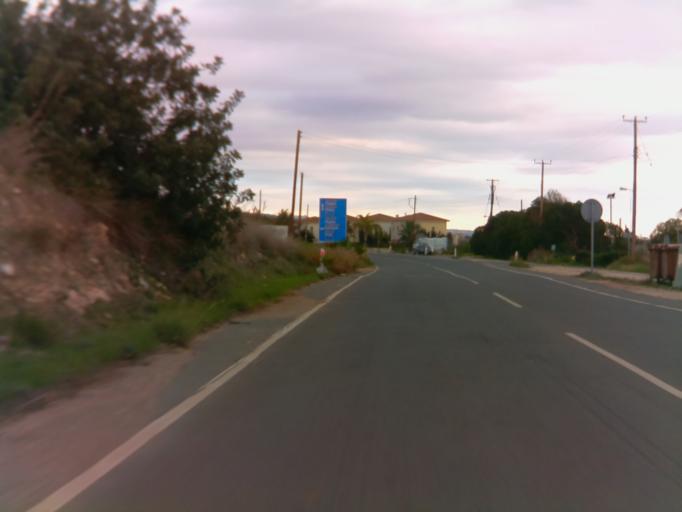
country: CY
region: Pafos
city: Pegeia
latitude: 34.8852
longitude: 32.3421
